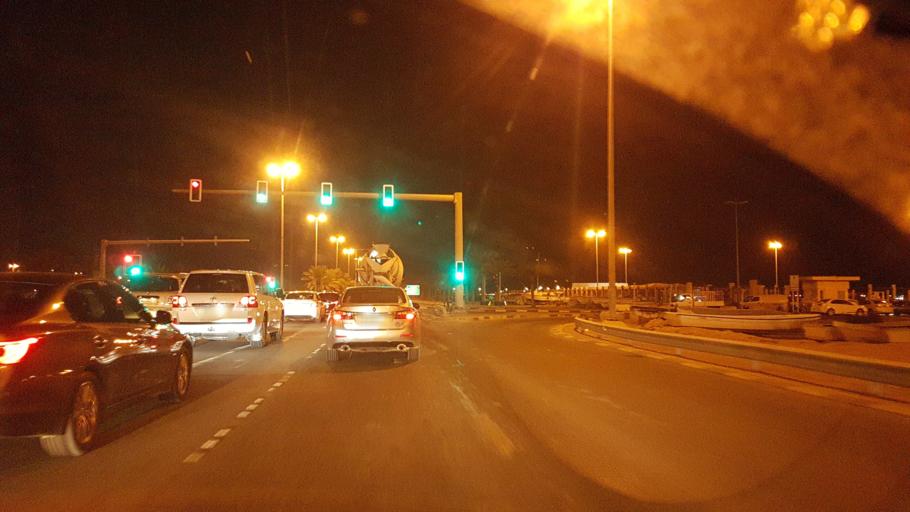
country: BH
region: Muharraq
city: Al Hadd
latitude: 26.2444
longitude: 50.6584
